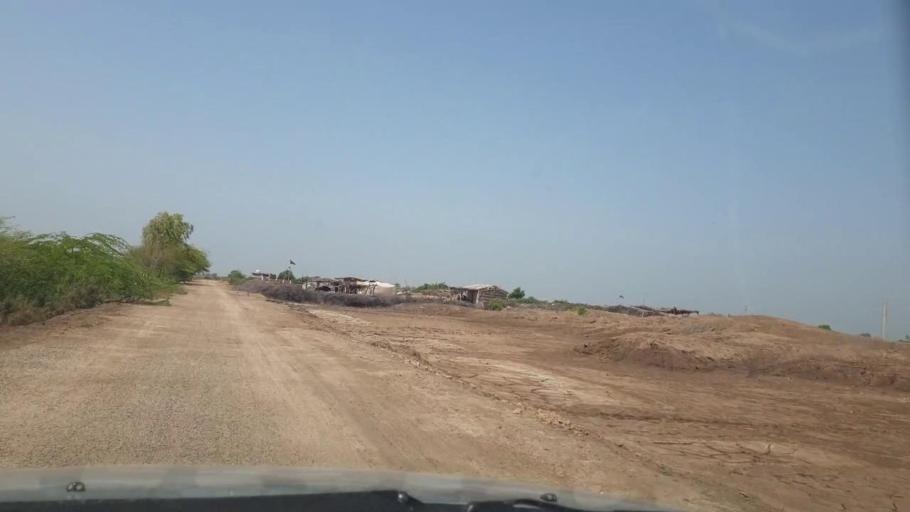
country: PK
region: Sindh
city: Tando Ghulam Ali
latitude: 25.0748
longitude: 68.7938
